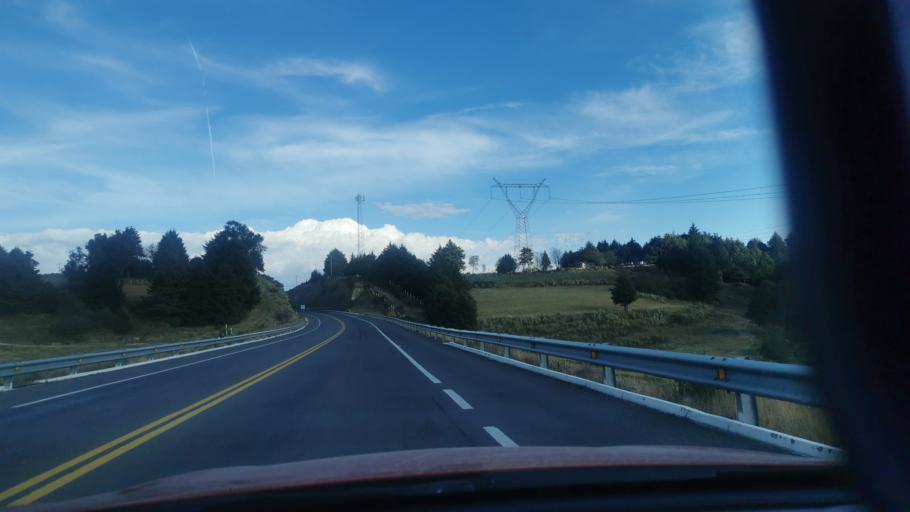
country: MX
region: Mexico
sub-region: Villa Victoria
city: Colonia Doctor Gustavo Baz
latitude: 19.3724
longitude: -99.9194
